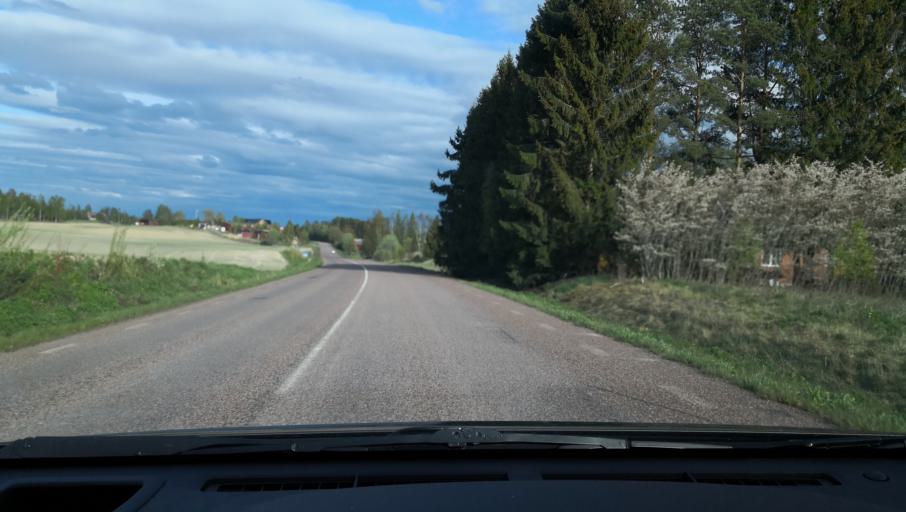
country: SE
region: Dalarna
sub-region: Hedemora Kommun
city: Hedemora
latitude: 60.2858
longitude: 15.9177
